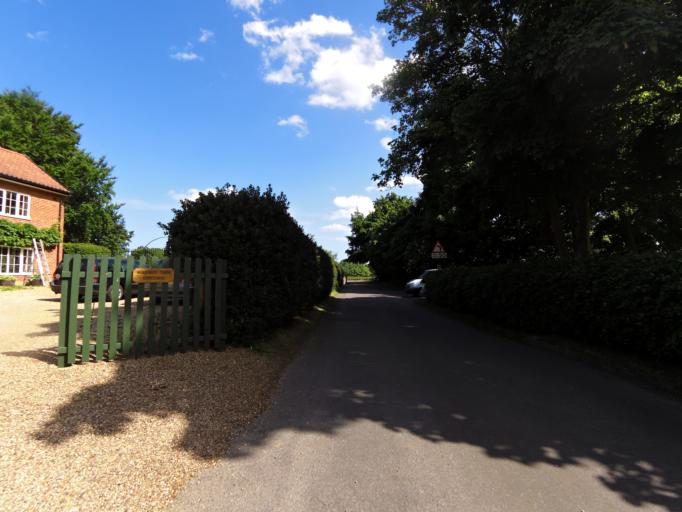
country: GB
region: England
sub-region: Suffolk
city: Shotley Gate
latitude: 52.0051
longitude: 1.2530
